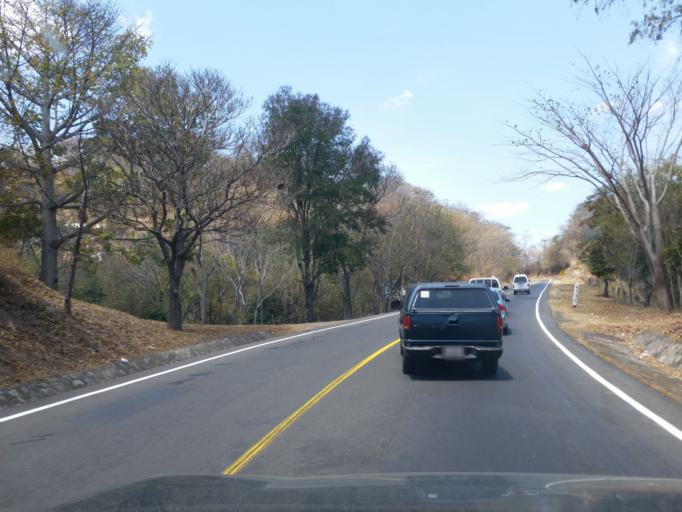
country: NI
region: Esteli
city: Esteli
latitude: 12.9945
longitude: -86.2793
